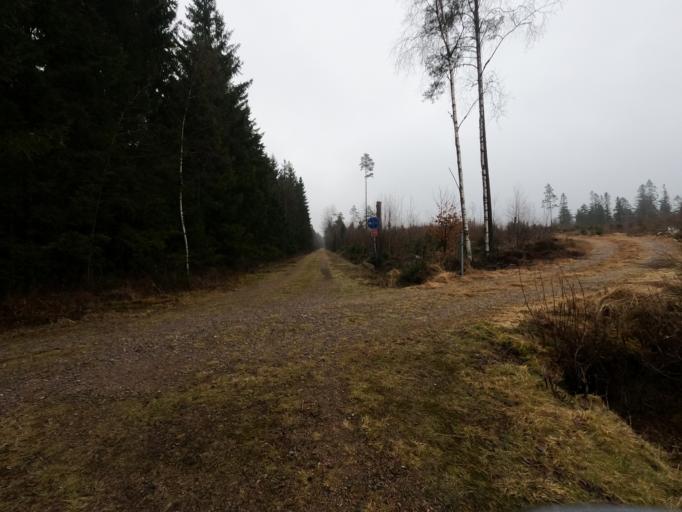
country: SE
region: Halland
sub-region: Hylte Kommun
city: Hyltebruk
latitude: 56.8116
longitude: 13.2750
